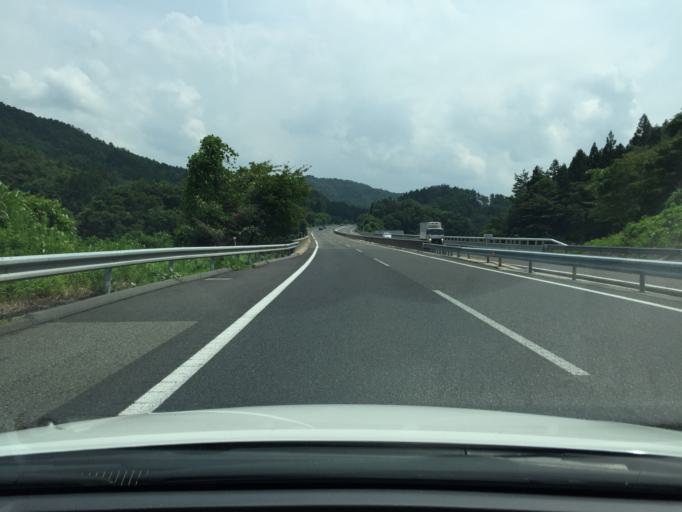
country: JP
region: Fukushima
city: Funehikimachi-funehiki
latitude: 37.4253
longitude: 140.5532
